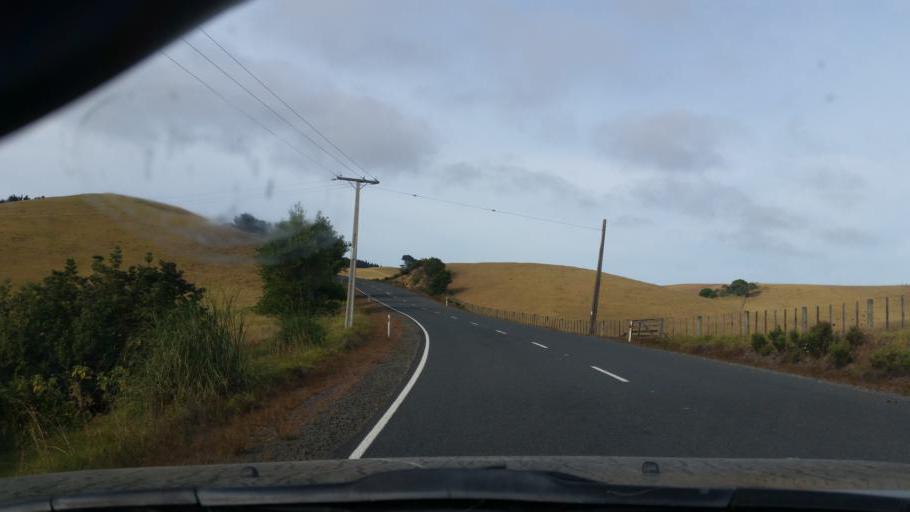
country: NZ
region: Northland
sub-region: Kaipara District
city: Dargaville
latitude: -36.2127
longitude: 174.0325
